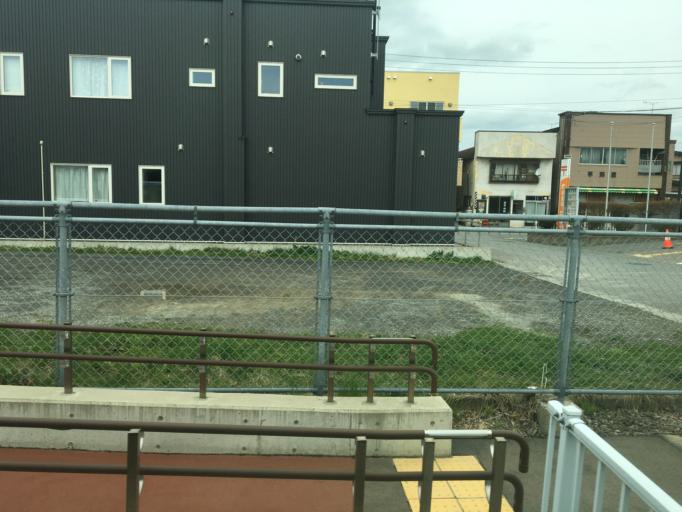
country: JP
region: Aomori
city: Shimokizukuri
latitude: 40.7759
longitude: 140.2211
